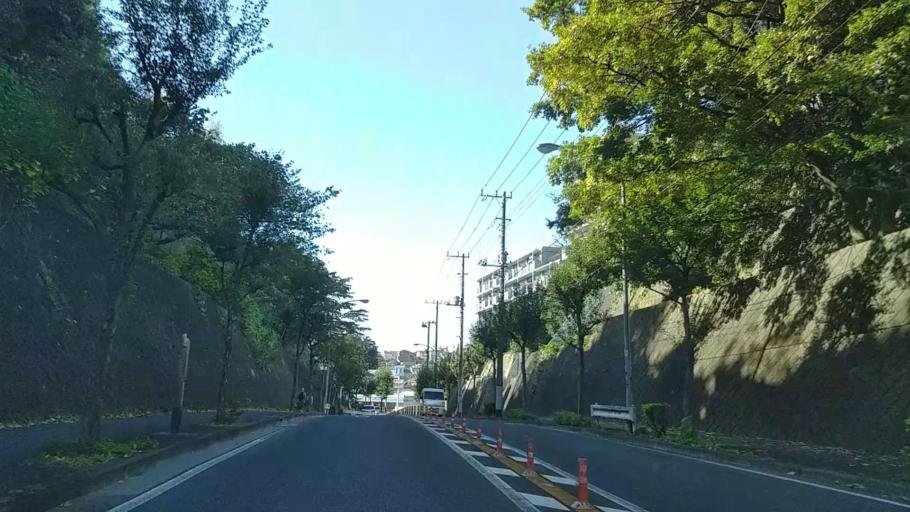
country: JP
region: Kanagawa
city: Yokohama
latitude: 35.4243
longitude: 139.5762
